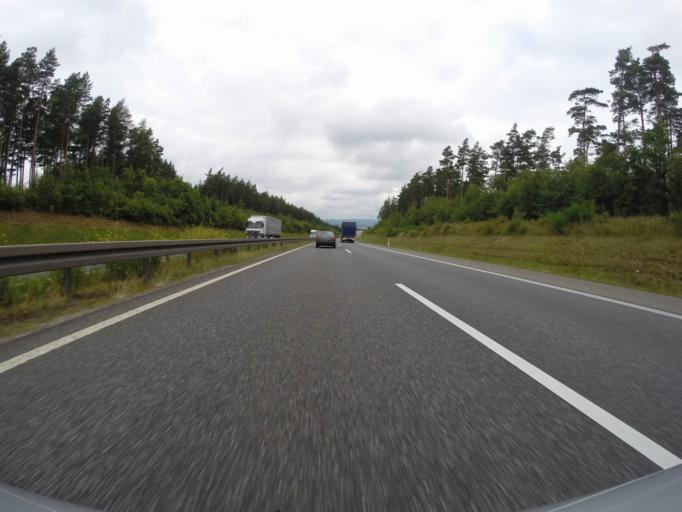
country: DE
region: Thuringia
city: Martinroda
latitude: 50.7126
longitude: 10.8836
